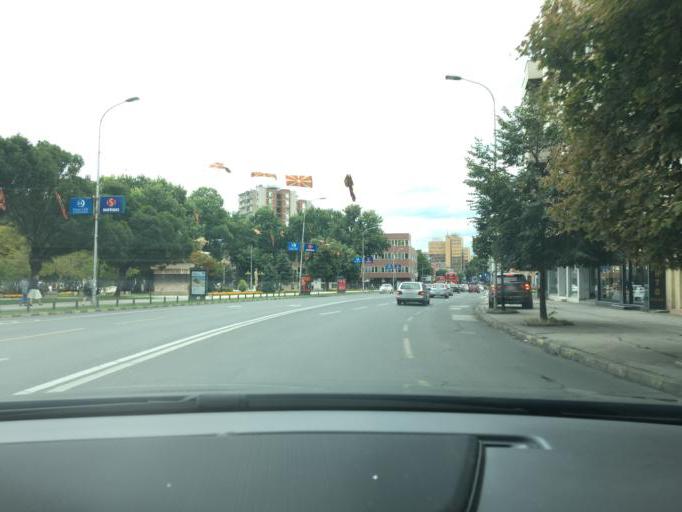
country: MK
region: Karpos
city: Skopje
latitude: 41.9941
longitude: 21.4324
